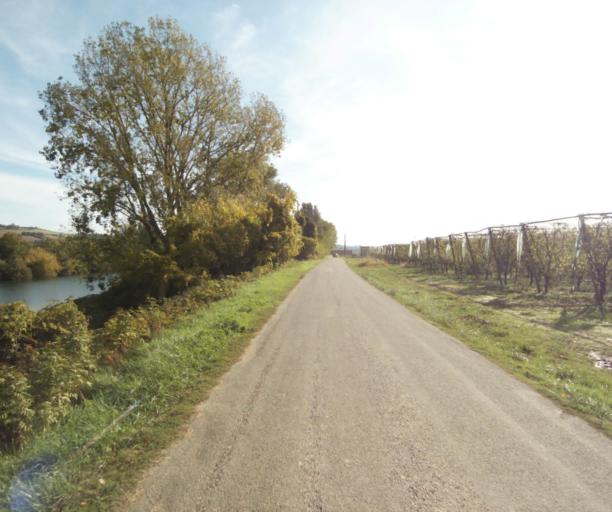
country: FR
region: Midi-Pyrenees
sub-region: Departement du Tarn-et-Garonne
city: Nohic
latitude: 43.9081
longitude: 1.4333
